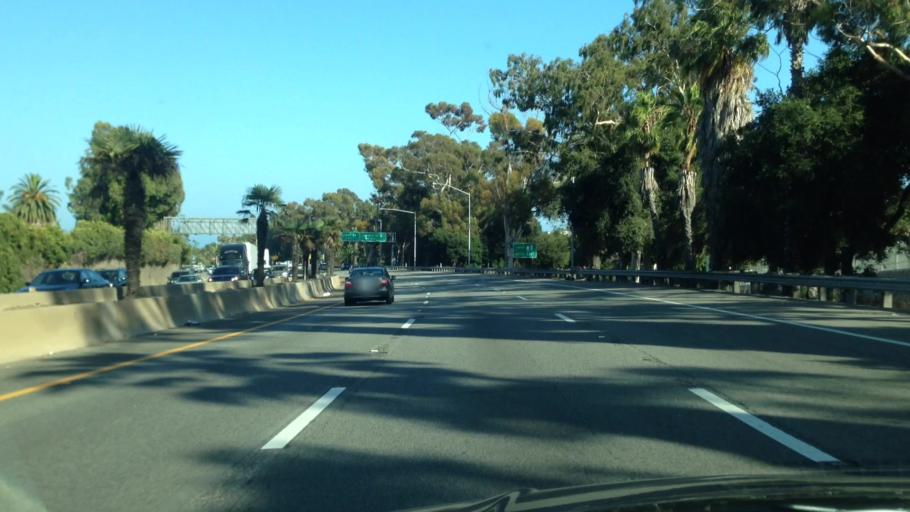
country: US
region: California
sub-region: Santa Barbara County
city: Santa Barbara
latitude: 34.4141
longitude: -119.7047
